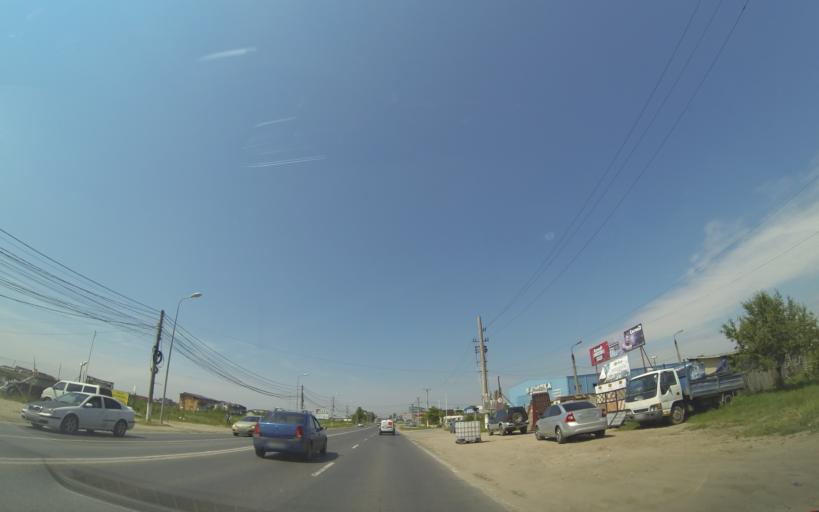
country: RO
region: Ilfov
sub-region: Comuna Magurele
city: Magurele
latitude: 44.3904
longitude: 26.0185
